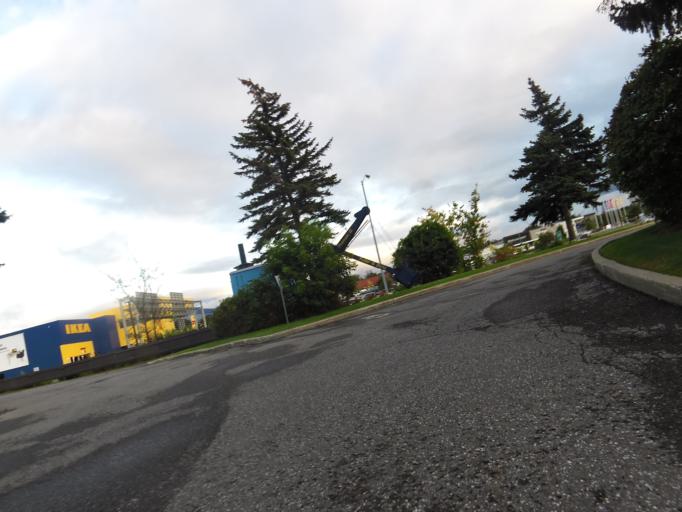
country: CA
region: Ontario
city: Bells Corners
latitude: 45.3517
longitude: -75.7873
